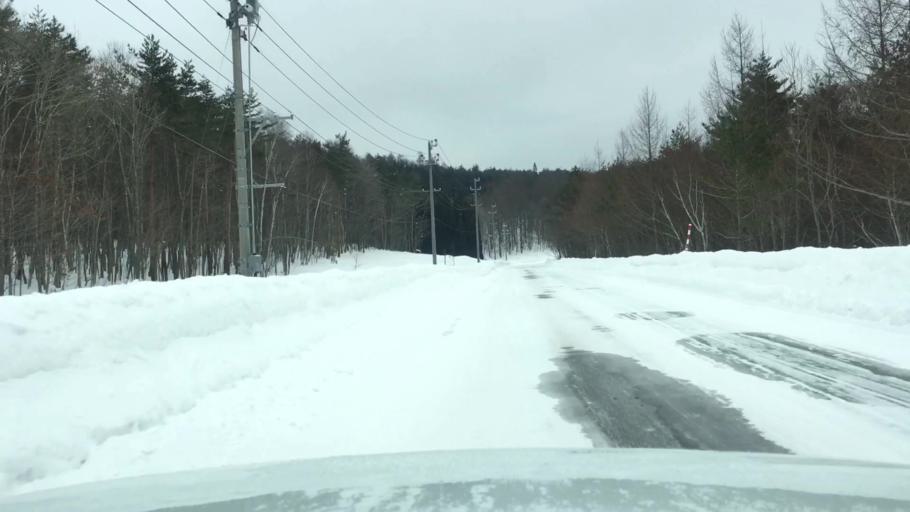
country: JP
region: Iwate
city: Shizukuishi
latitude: 39.9767
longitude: 141.0006
